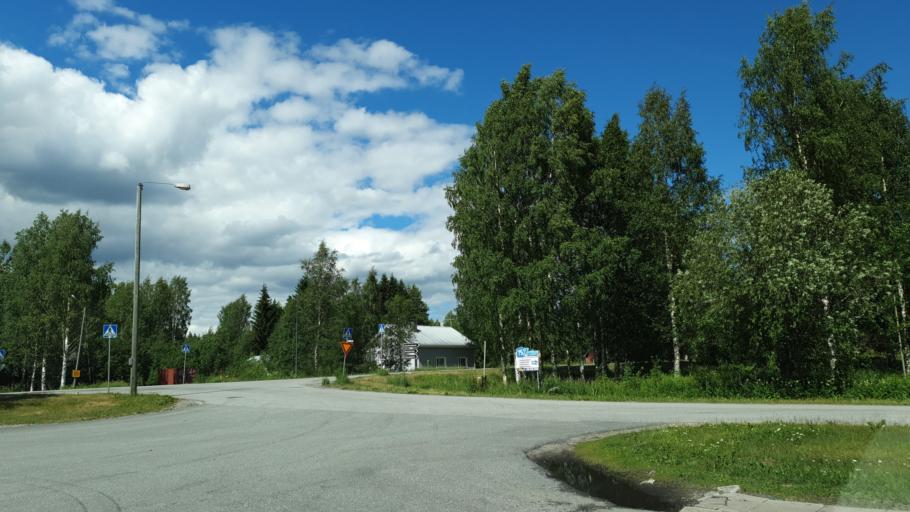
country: FI
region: North Karelia
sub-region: Pielisen Karjala
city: Nurmes
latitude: 63.5535
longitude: 29.0992
